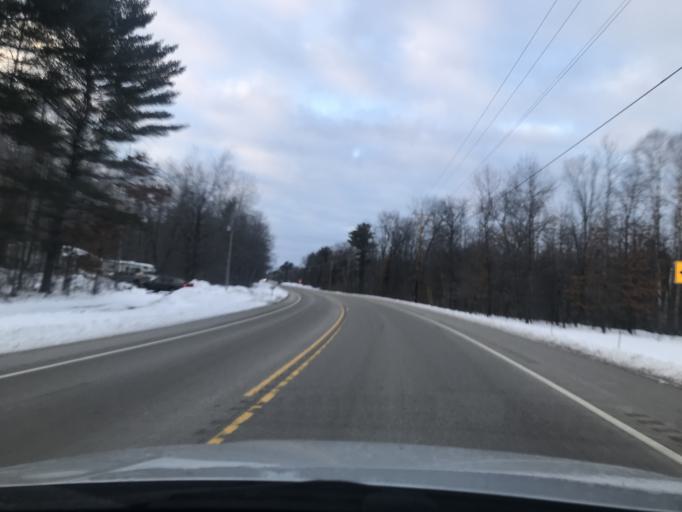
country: US
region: Wisconsin
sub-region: Marinette County
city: Marinette
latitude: 45.1402
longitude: -87.6915
